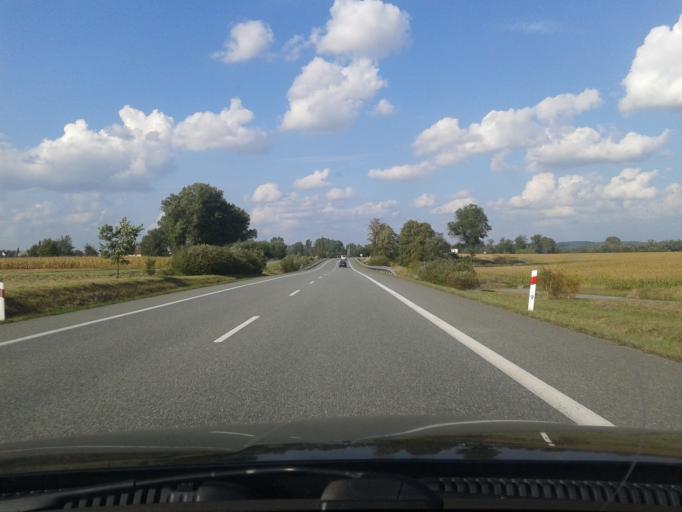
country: PL
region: Silesian Voivodeship
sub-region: Powiat raciborski
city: Chalupki
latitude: 49.9313
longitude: 18.3245
